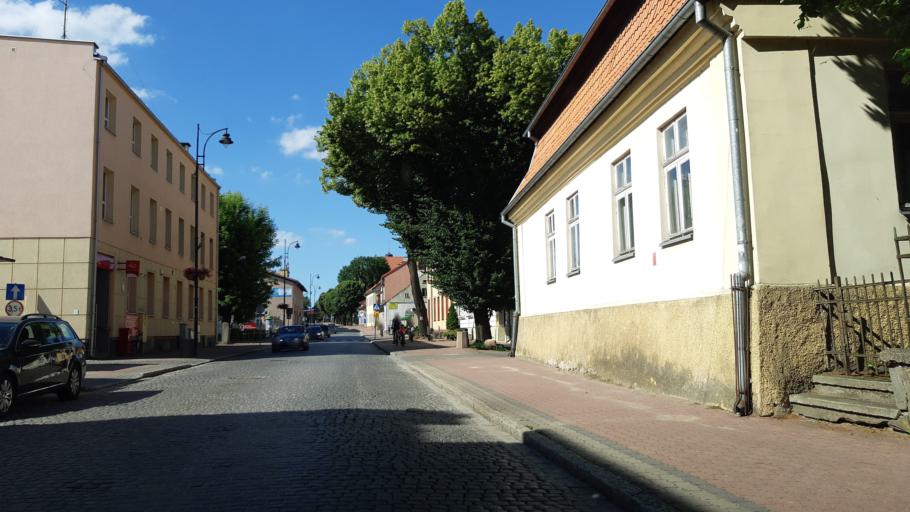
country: PL
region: Warmian-Masurian Voivodeship
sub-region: Powiat mragowski
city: Mragowo
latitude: 53.8736
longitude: 21.3040
